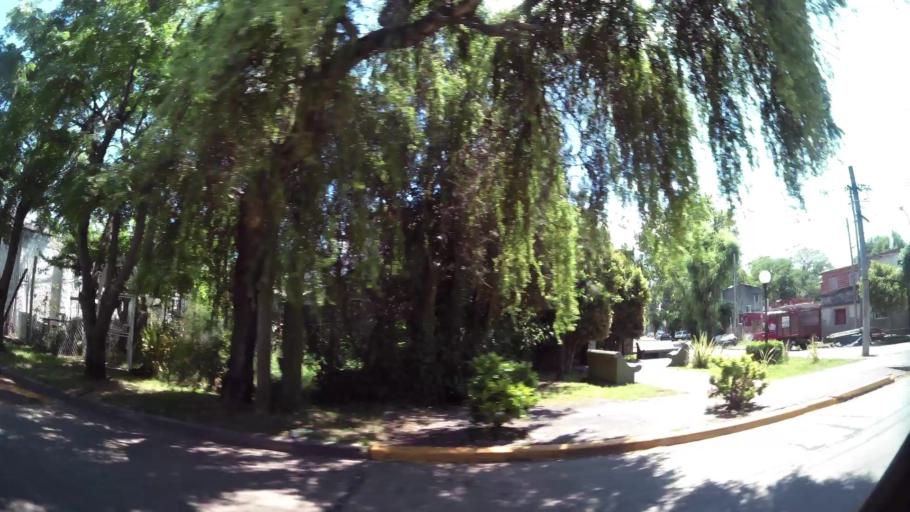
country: AR
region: Buenos Aires
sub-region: Partido de Tigre
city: Tigre
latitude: -34.4340
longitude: -58.5766
